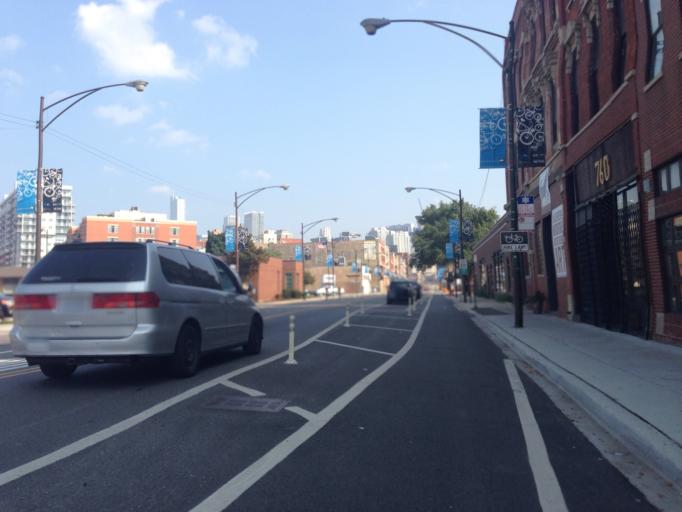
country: US
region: Illinois
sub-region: Cook County
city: Chicago
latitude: 41.8958
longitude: -87.6549
